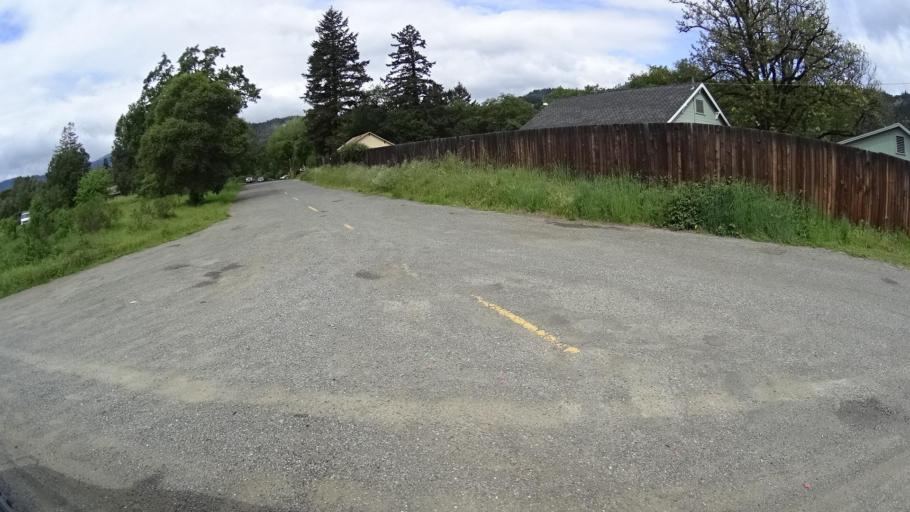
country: US
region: California
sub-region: Humboldt County
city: Redway
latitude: 40.1755
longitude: -123.6105
